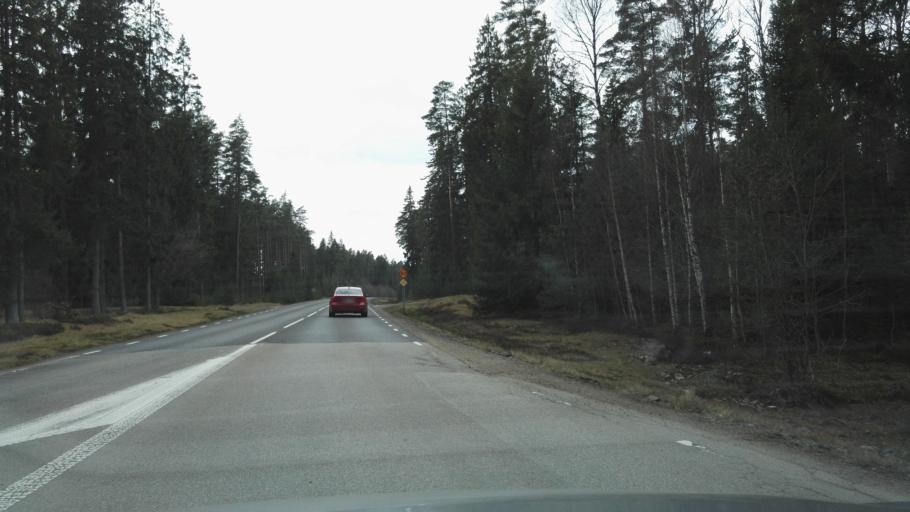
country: SE
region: Kronoberg
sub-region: Vaxjo Kommun
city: Braas
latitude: 57.0544
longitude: 15.0593
